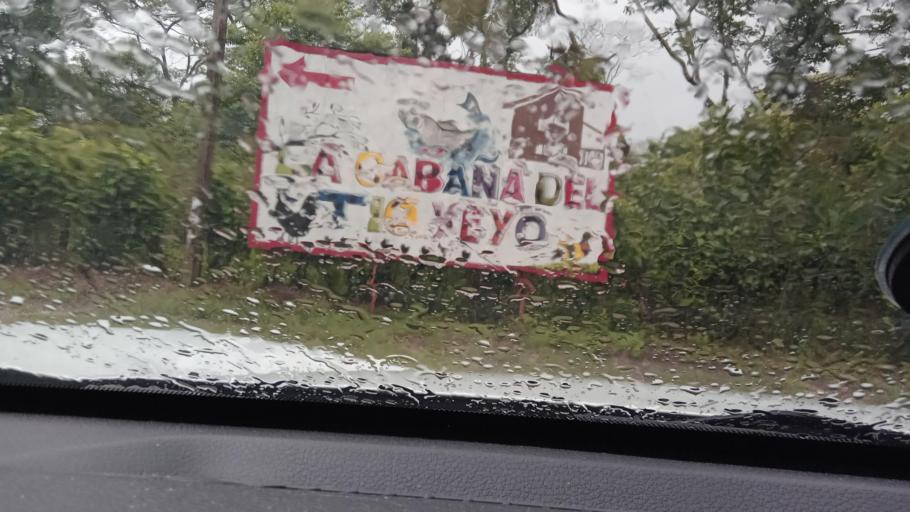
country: MX
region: Veracruz
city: Coatepec
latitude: 19.4546
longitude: -96.9794
